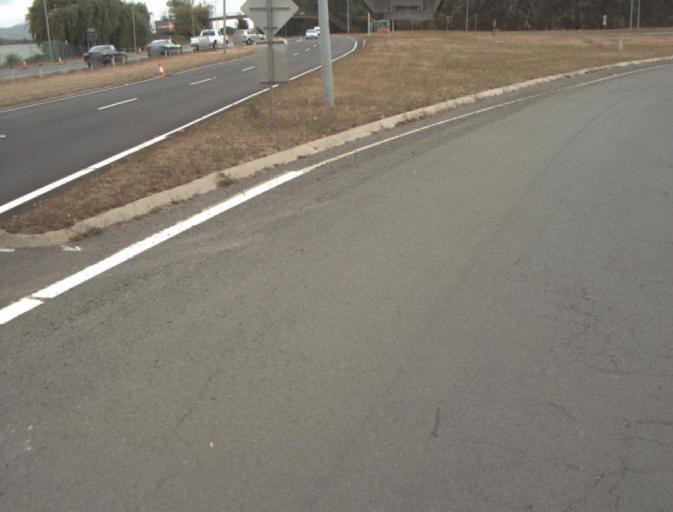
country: AU
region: Tasmania
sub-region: Launceston
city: Newnham
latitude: -41.4116
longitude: 147.1290
